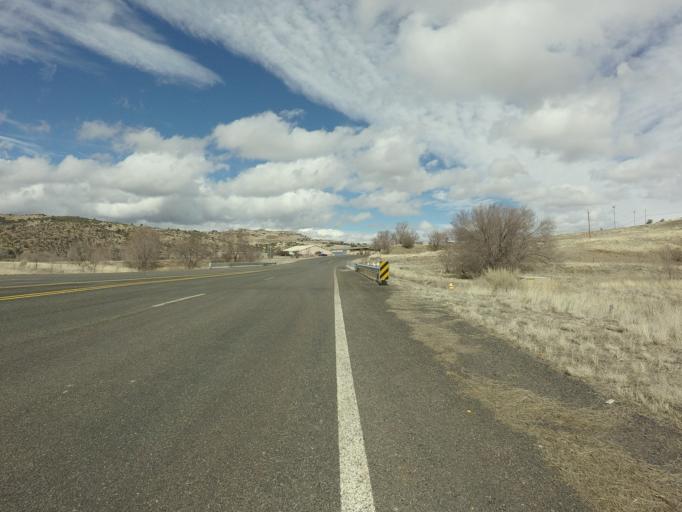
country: US
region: Arizona
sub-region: Yavapai County
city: Prescott
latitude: 34.5605
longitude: -112.4409
